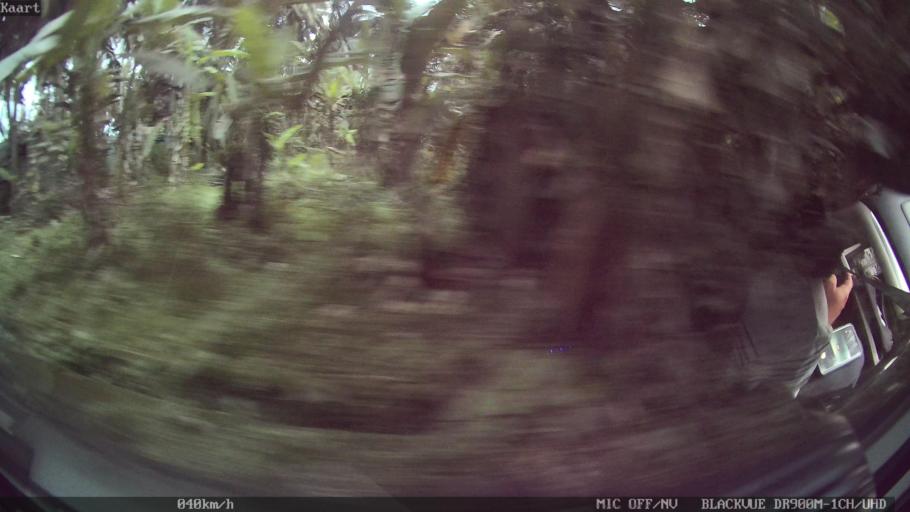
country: ID
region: Bali
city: Banjar Parekan
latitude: -8.5767
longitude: 115.2113
